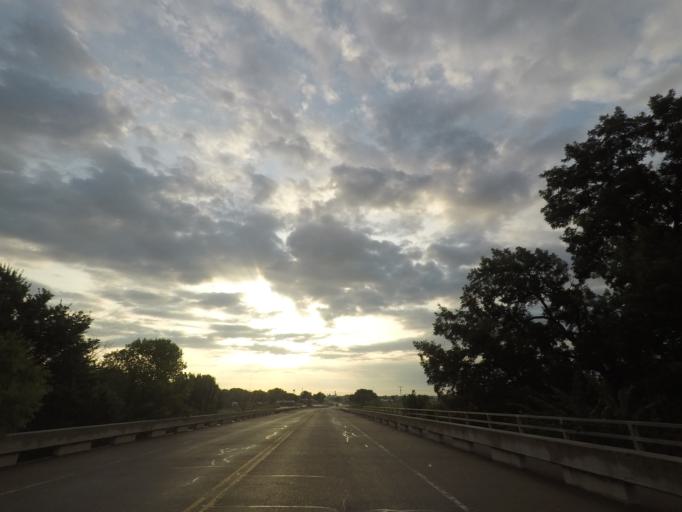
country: US
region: Oklahoma
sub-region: Jefferson County
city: Waurika
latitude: 34.1586
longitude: -98.0047
